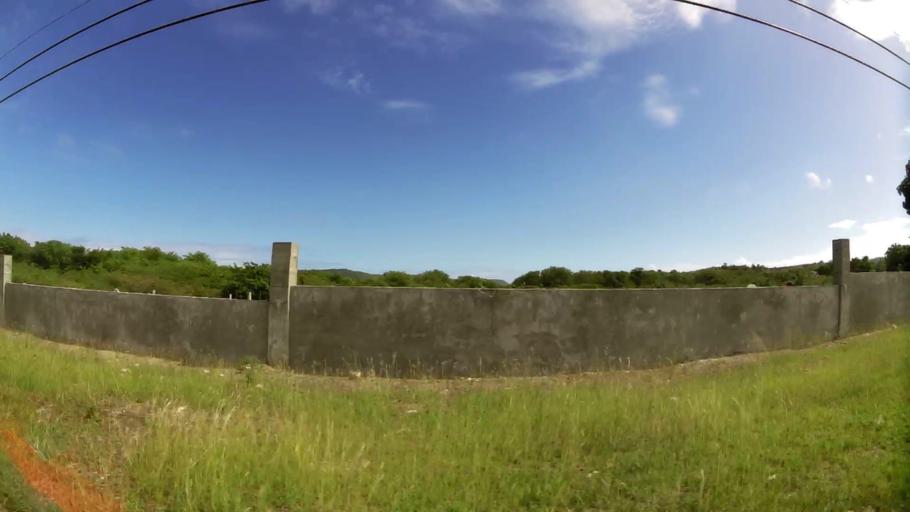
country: AG
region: Saint Paul
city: Falmouth
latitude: 17.0398
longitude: -61.7511
